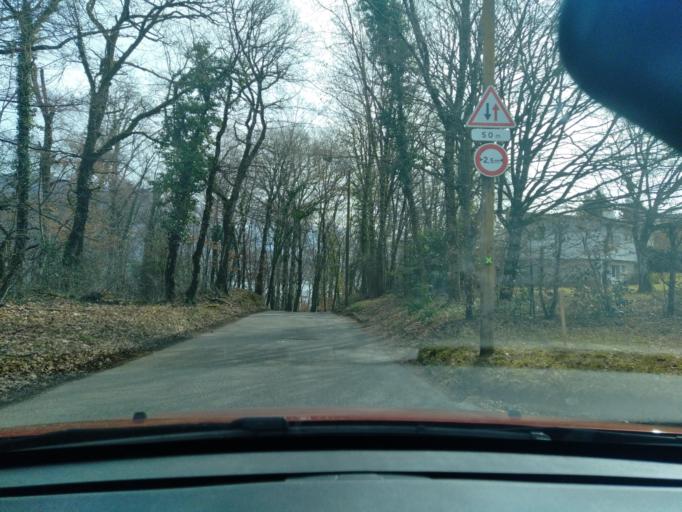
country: FR
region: Rhone-Alpes
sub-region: Departement de la Haute-Savoie
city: Sevrier
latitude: 45.8869
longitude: 6.1402
